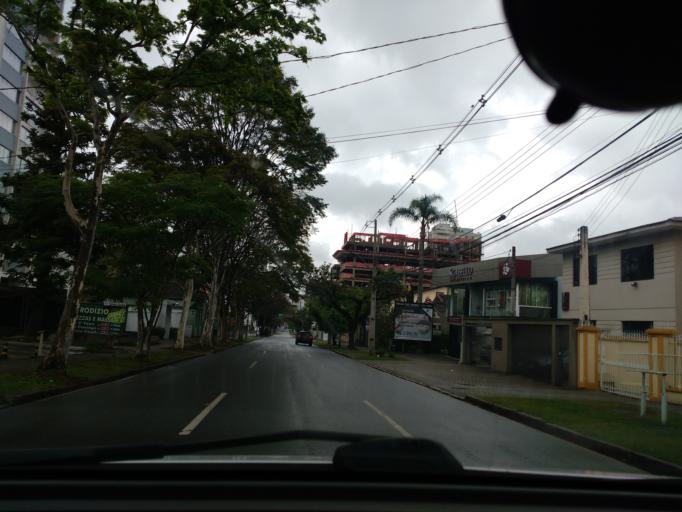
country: BR
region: Parana
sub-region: Curitiba
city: Curitiba
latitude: -25.4270
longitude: -49.2870
